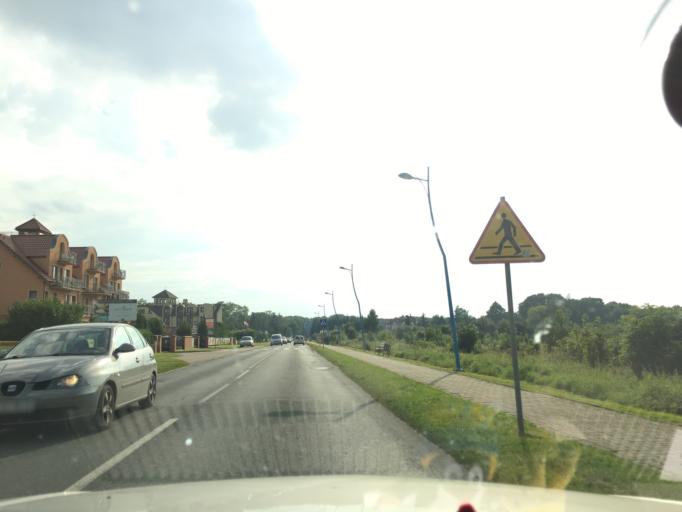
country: PL
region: West Pomeranian Voivodeship
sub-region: Powiat gryficki
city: Rewal
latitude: 54.0780
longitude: 14.9995
